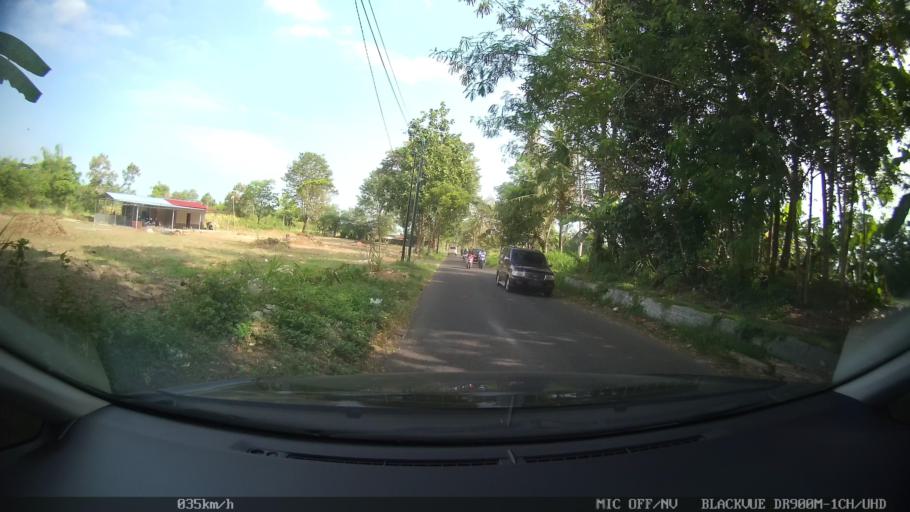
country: ID
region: Daerah Istimewa Yogyakarta
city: Depok
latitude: -7.7240
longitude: 110.4397
